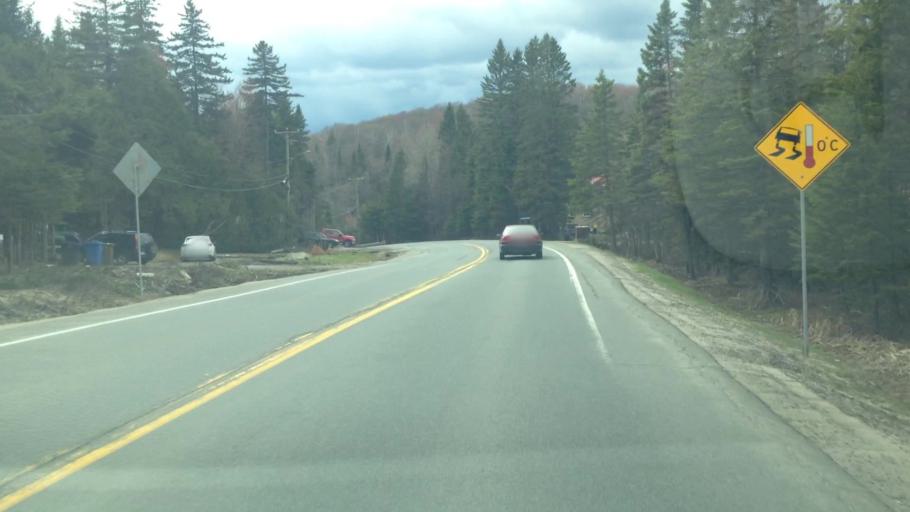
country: CA
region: Quebec
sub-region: Laurentides
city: Sainte-Adele
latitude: 46.0190
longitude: -74.0839
